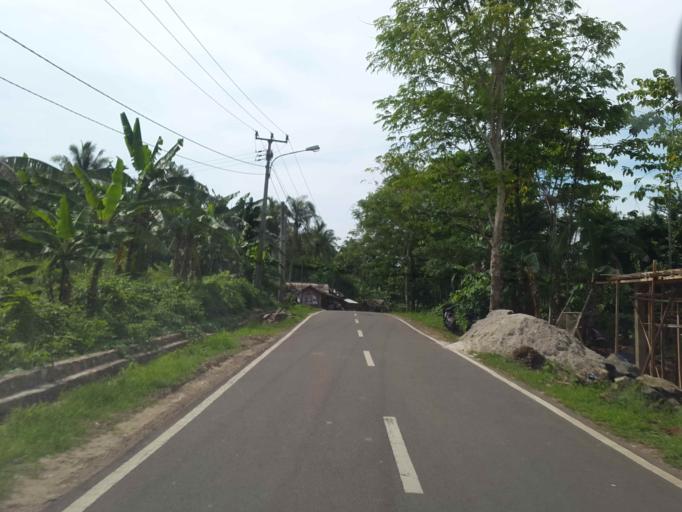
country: ID
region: Banten
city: Citeureup
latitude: -6.5188
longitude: 105.6846
